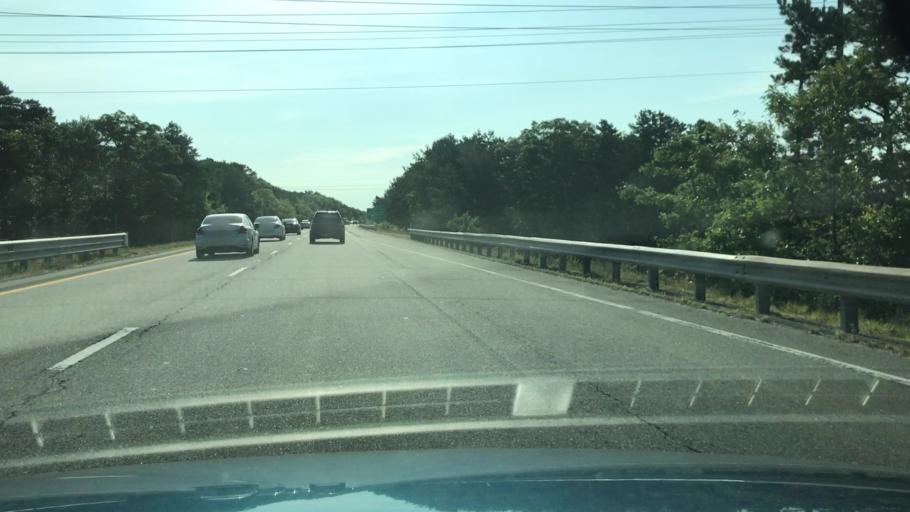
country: US
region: Massachusetts
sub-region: Barnstable County
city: Barnstable
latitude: 41.6872
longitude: -70.2847
